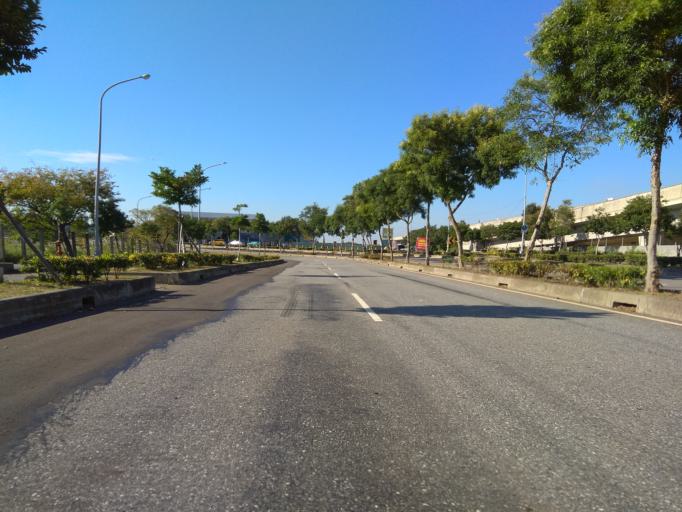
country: TW
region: Taiwan
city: Taoyuan City
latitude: 25.0249
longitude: 121.2195
